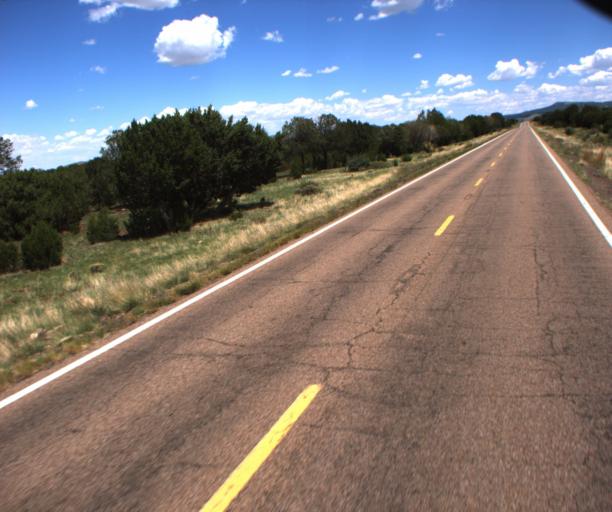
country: US
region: Arizona
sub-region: Navajo County
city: Pinetop-Lakeside
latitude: 34.2702
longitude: -109.7244
